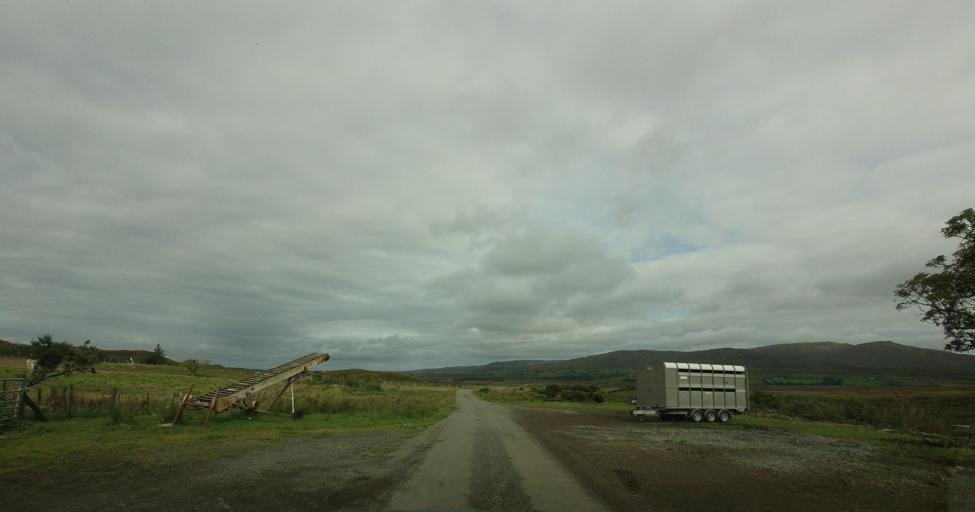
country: GB
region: Scotland
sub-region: Highland
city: Isle of Skye
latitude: 57.4187
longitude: -6.2575
